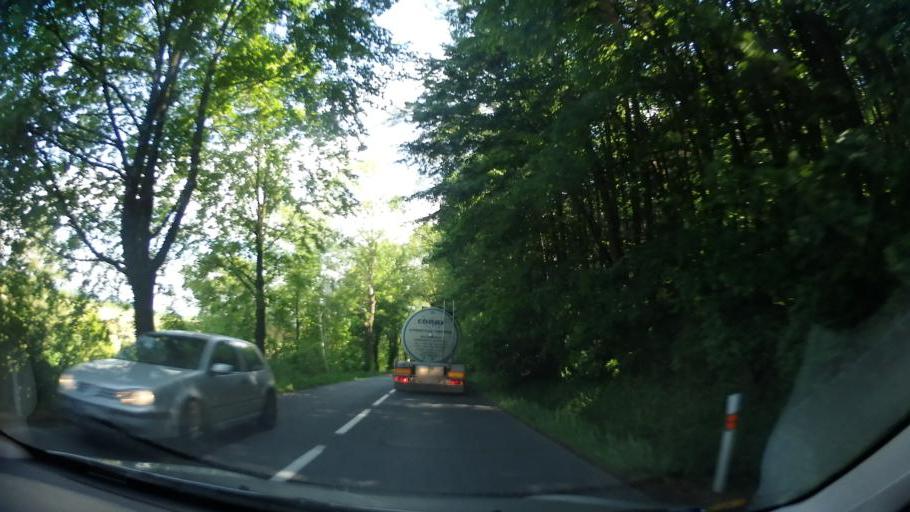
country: CZ
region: Pardubicky
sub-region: Okres Svitavy
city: Moravska Trebova
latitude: 49.7251
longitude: 16.6408
